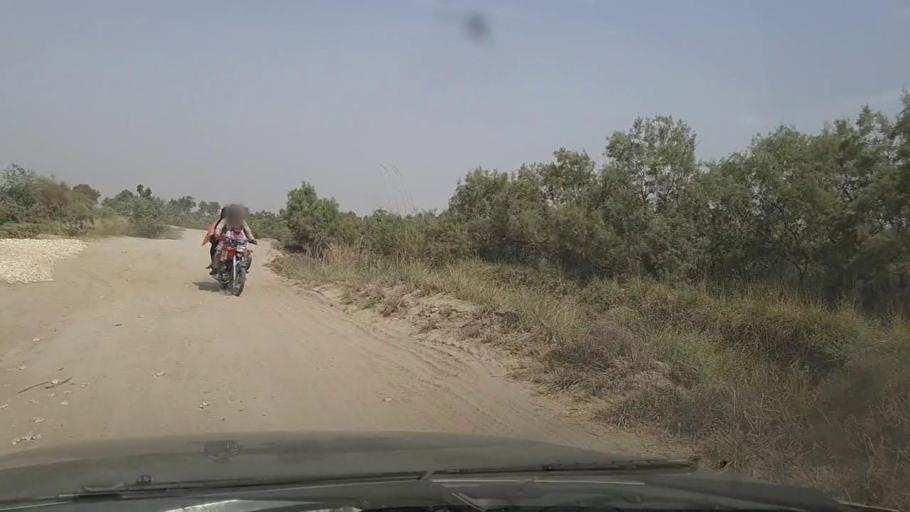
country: PK
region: Sindh
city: Thul
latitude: 28.4002
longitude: 68.7085
